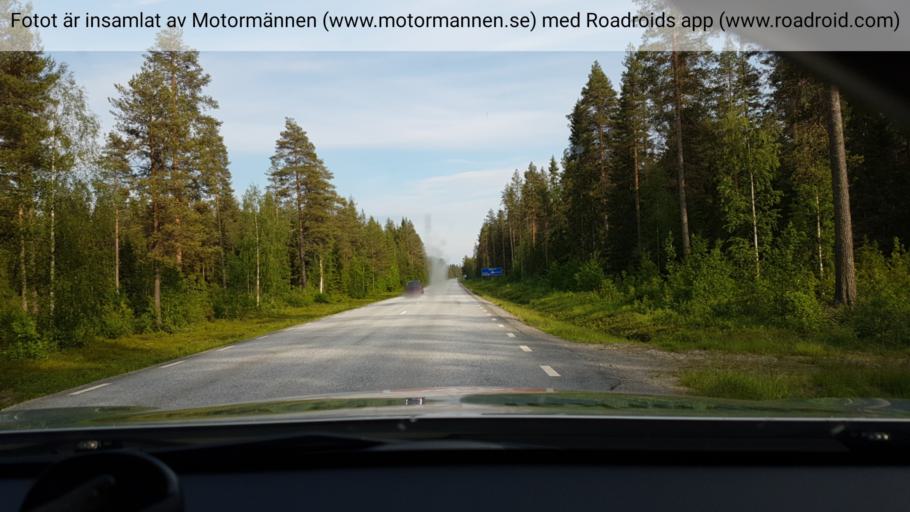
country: SE
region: Vaesterbotten
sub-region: Vindelns Kommun
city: Vindeln
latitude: 64.0884
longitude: 19.6200
